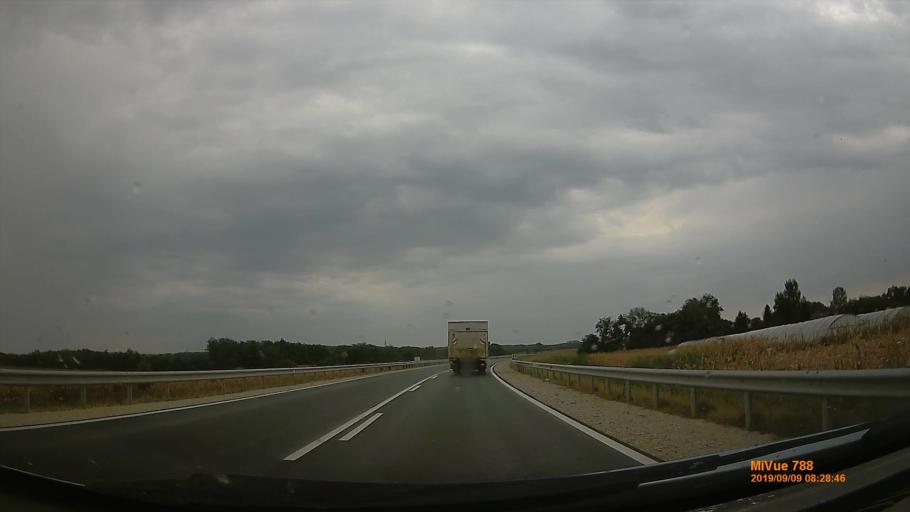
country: HU
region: Szabolcs-Szatmar-Bereg
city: Kalmanhaza
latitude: 47.9232
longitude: 21.6430
